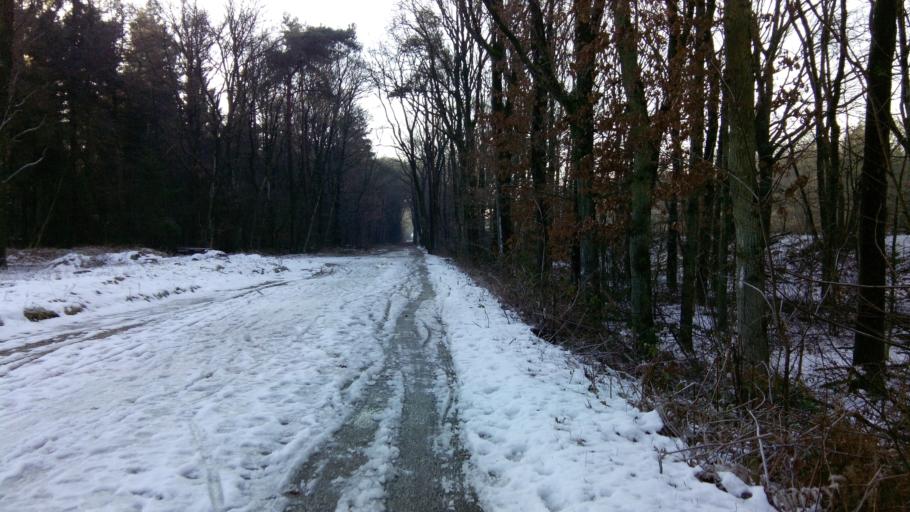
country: NL
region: Gelderland
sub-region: Gemeente Groesbeek
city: Berg en Dal
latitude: 51.7931
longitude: 5.8875
